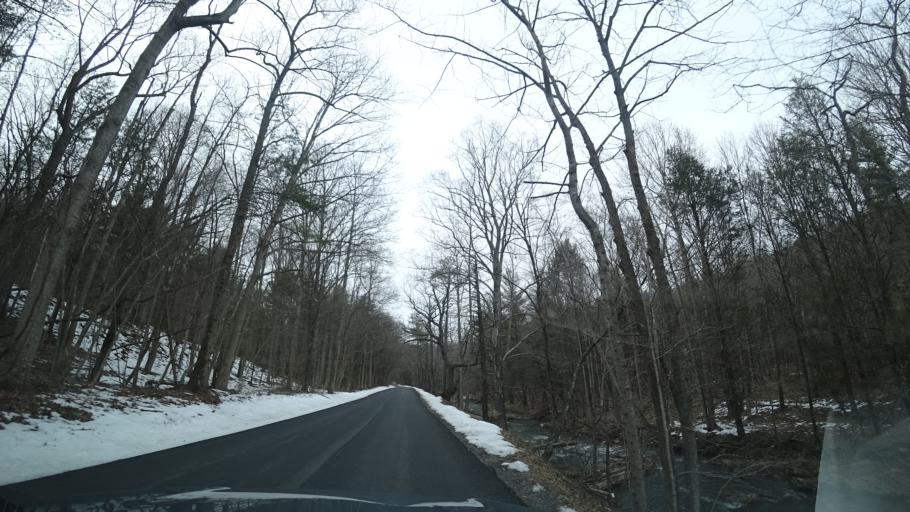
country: US
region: Virginia
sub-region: Shenandoah County
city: Woodstock
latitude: 39.0068
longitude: -78.6633
